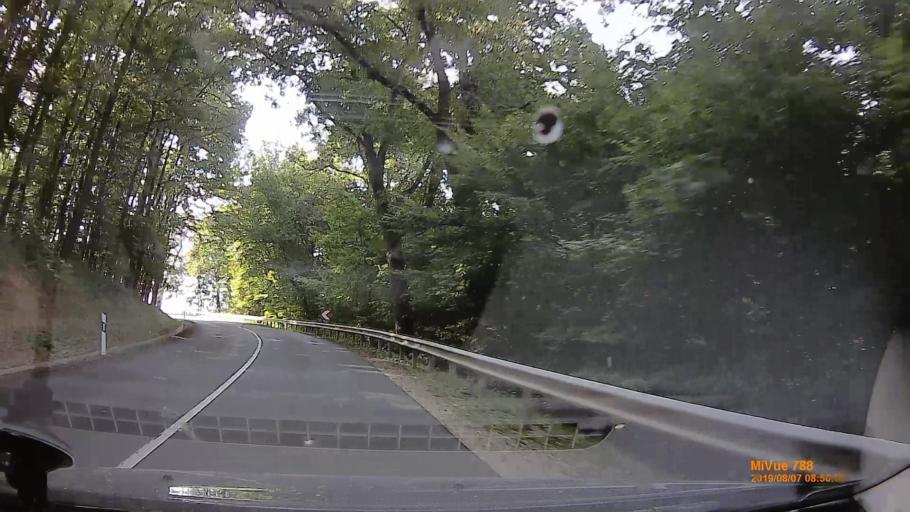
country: HU
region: Zala
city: Zalaegerszeg
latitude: 46.7319
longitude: 16.8856
